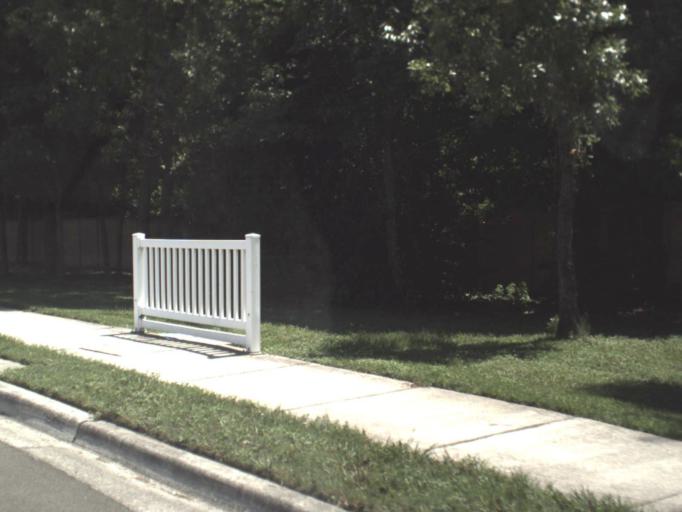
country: US
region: Florida
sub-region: Saint Johns County
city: Fruit Cove
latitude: 30.0931
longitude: -81.6279
